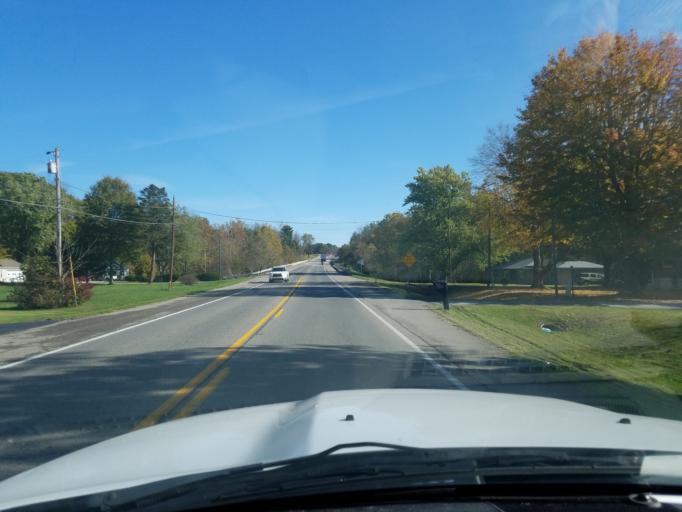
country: US
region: Indiana
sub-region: Jennings County
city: North Vernon
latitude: 39.0070
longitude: -85.6072
